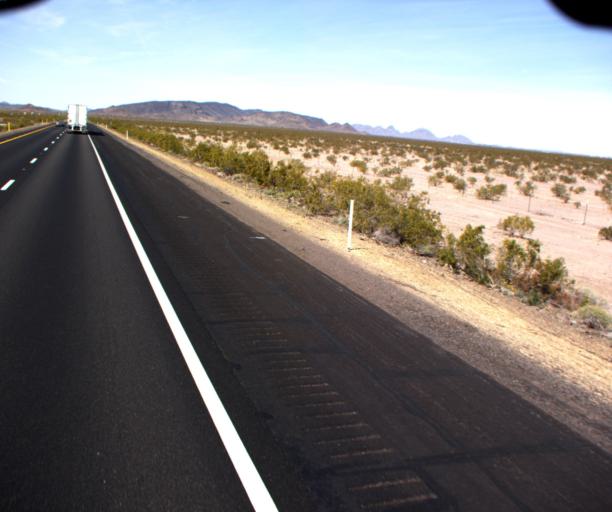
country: US
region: Arizona
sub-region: La Paz County
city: Salome
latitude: 33.6393
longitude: -113.8227
